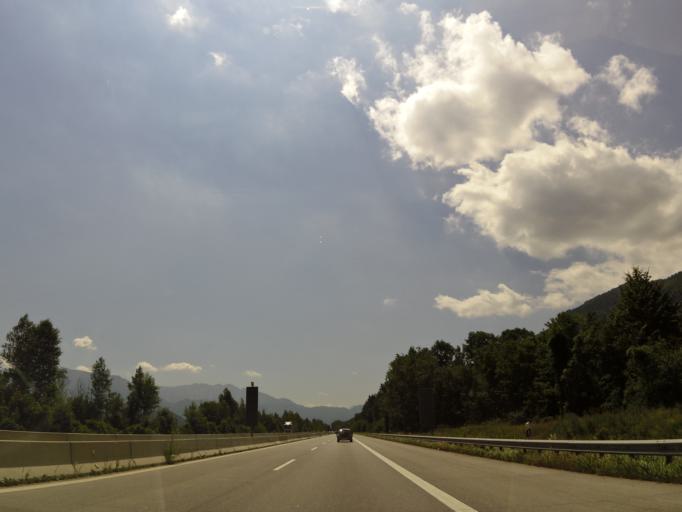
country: AT
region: Tyrol
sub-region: Politischer Bezirk Kufstein
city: Erl
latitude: 47.6954
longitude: 12.1622
